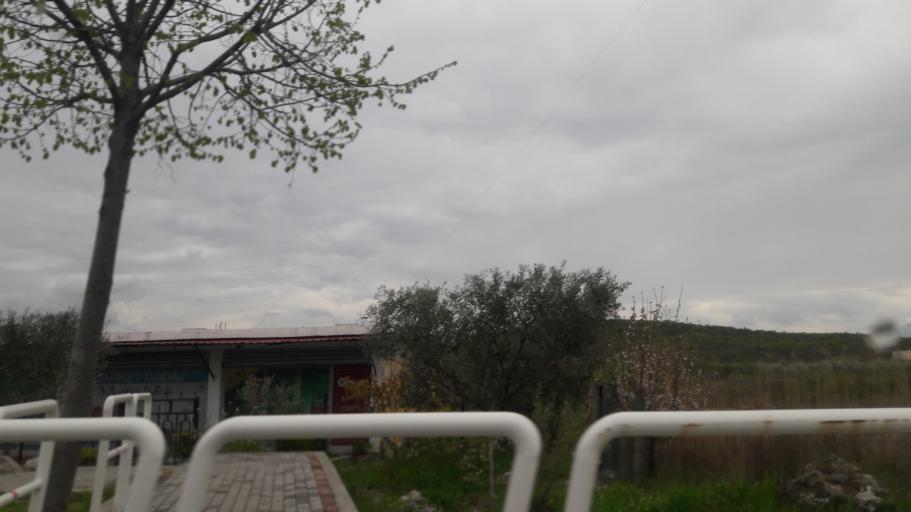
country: AL
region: Shkoder
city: Vukatane
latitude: 41.9646
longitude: 19.5380
